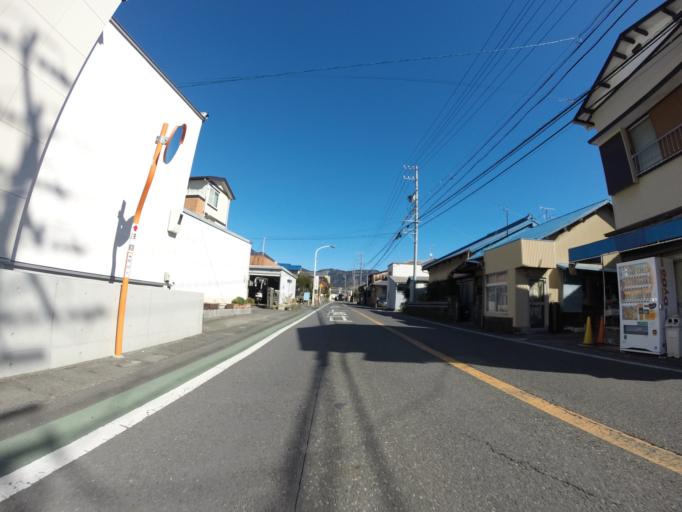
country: JP
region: Shizuoka
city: Shizuoka-shi
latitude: 35.0221
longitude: 138.3883
